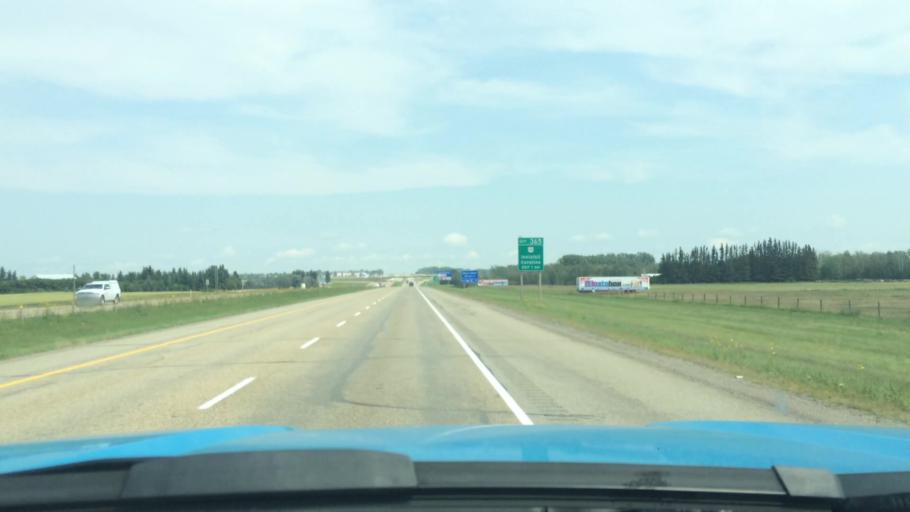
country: CA
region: Alberta
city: Penhold
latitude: 51.9931
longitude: -113.9756
